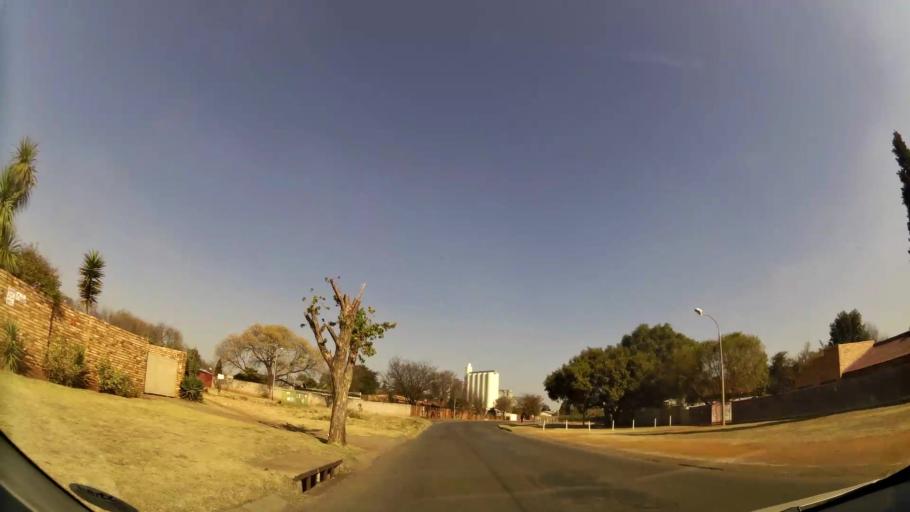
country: ZA
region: Gauteng
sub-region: West Rand District Municipality
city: Randfontein
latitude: -26.1809
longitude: 27.6923
